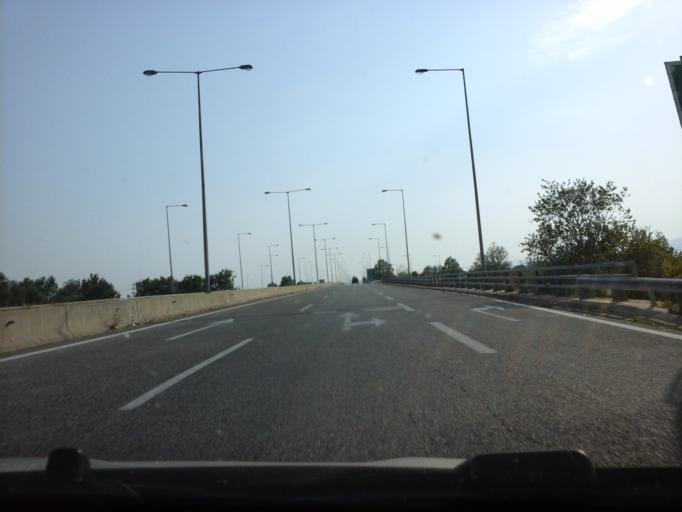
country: GR
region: East Macedonia and Thrace
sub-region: Nomos Xanthis
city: Genissea
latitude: 41.0993
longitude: 24.9500
